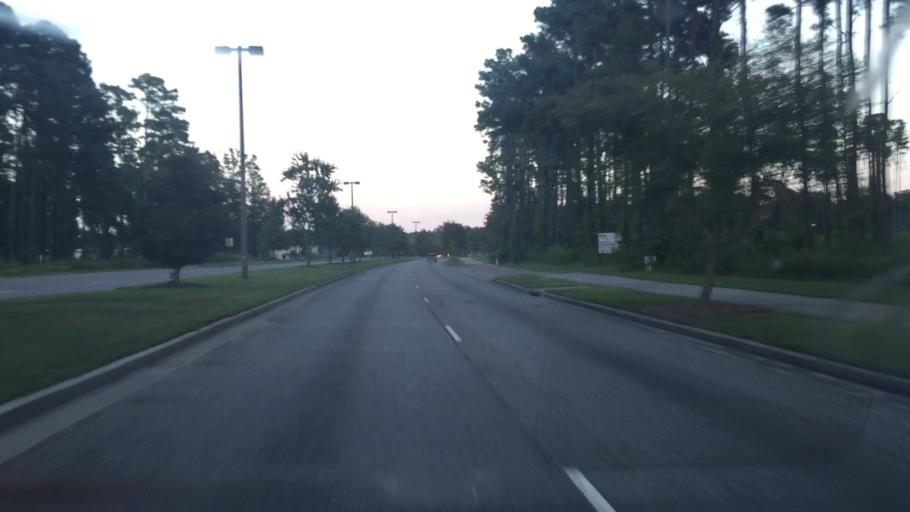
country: US
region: South Carolina
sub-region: Horry County
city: Myrtle Beach
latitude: 33.7032
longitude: -78.8978
